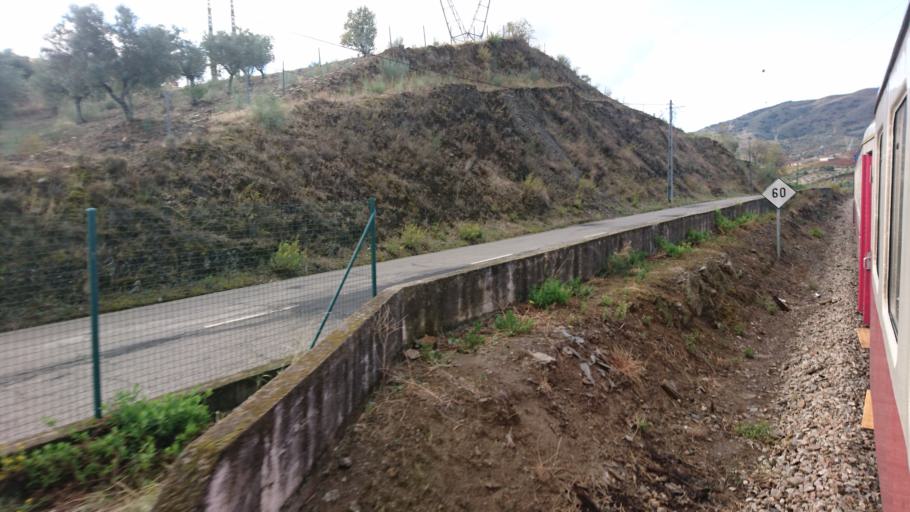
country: PT
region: Guarda
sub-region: Vila Nova de Foz Coa
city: Vila Nova de Foz Coa
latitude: 41.1281
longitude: -7.1292
